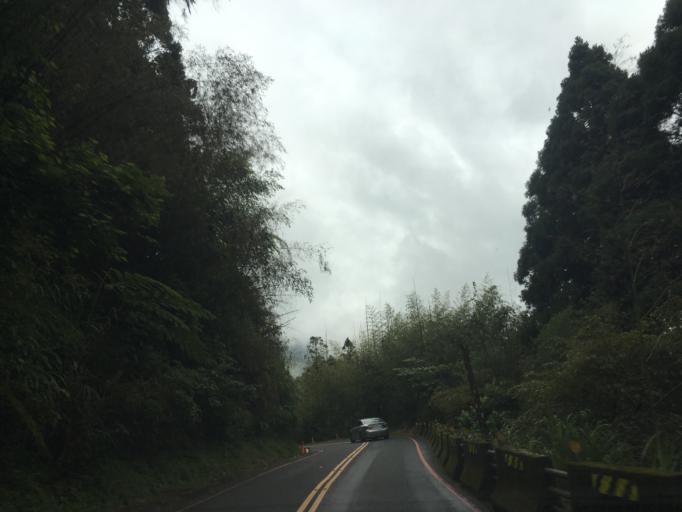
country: TW
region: Taiwan
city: Lugu
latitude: 23.5029
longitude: 120.6985
